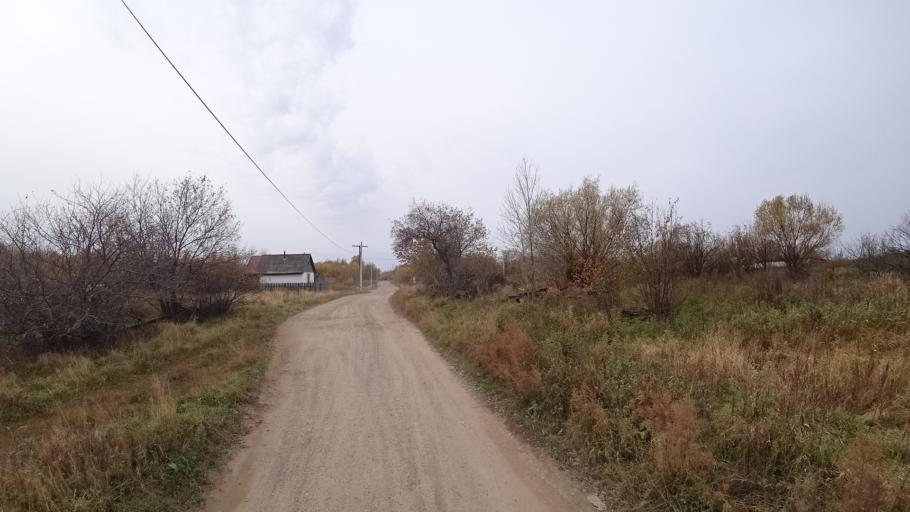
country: RU
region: Khabarovsk Krai
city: Amursk
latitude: 50.1408
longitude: 136.9585
